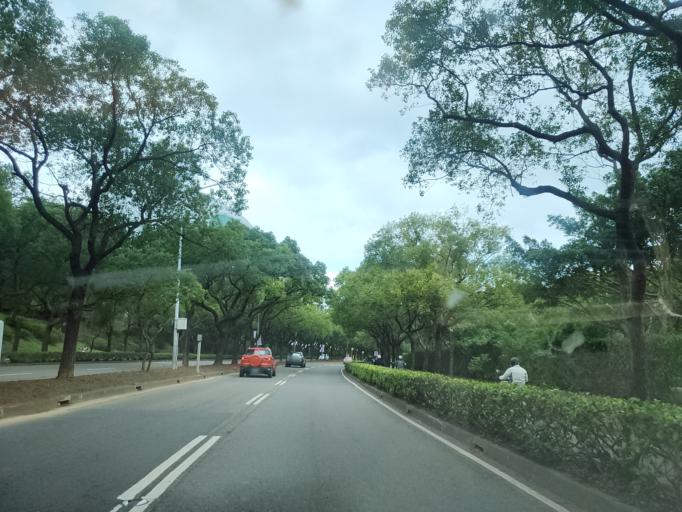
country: TW
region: Taiwan
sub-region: Hsinchu
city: Hsinchu
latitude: 24.7826
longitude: 121.0069
